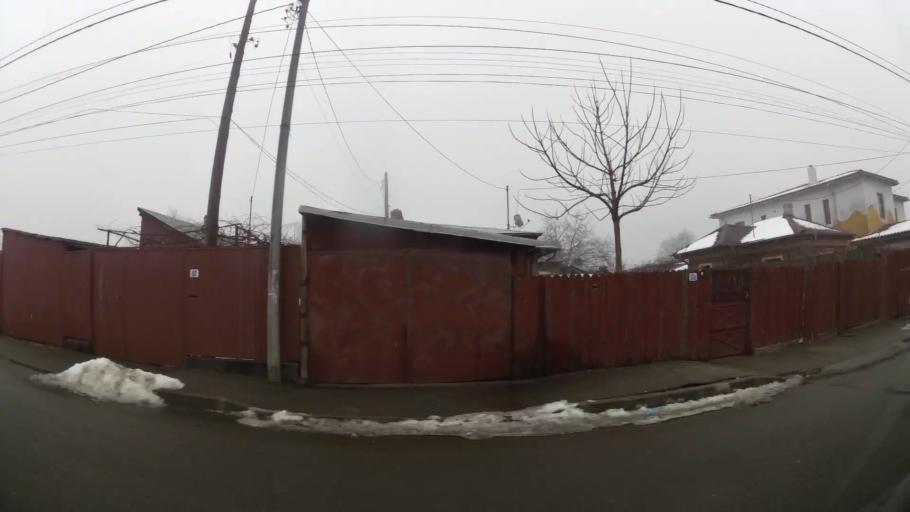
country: RO
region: Ilfov
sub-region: Comuna Chiajna
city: Rosu
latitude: 44.4756
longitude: 26.0053
